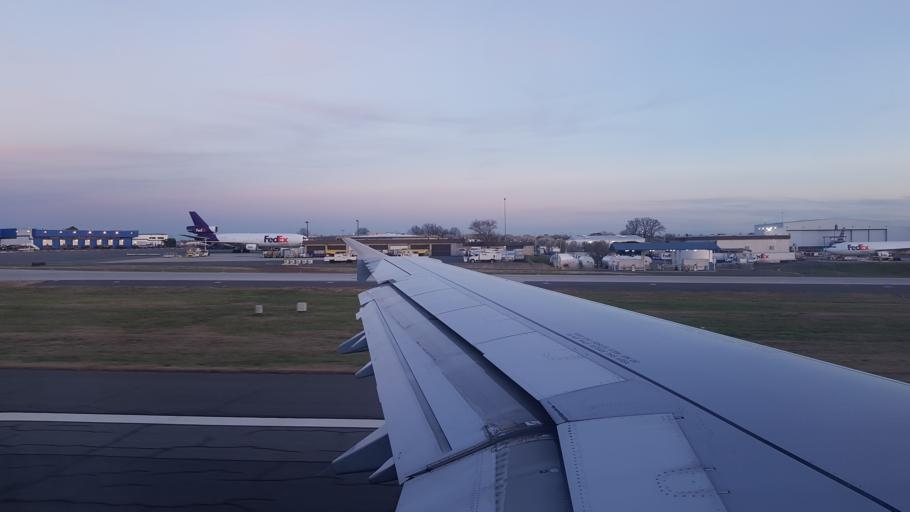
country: US
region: North Carolina
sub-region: Gaston County
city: Belmont
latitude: 35.2130
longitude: -80.9442
